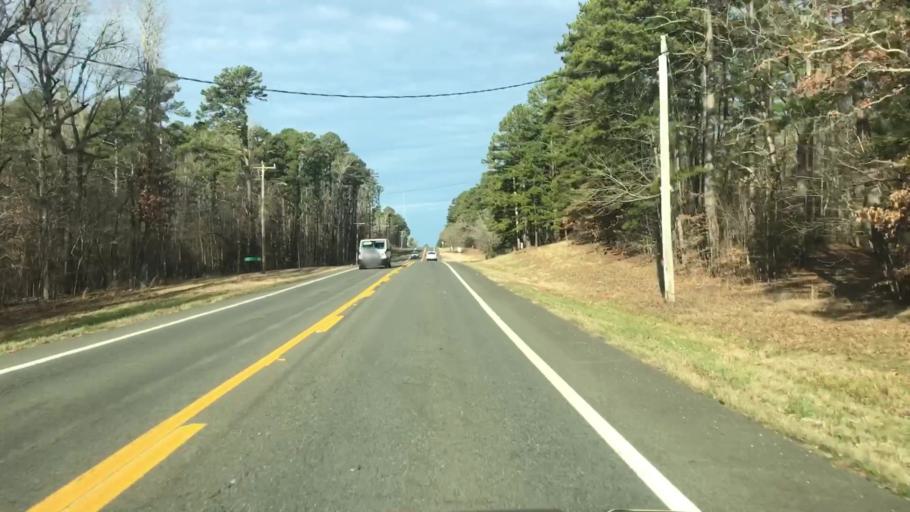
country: US
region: Arkansas
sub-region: Montgomery County
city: Mount Ida
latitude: 34.5411
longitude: -93.6078
